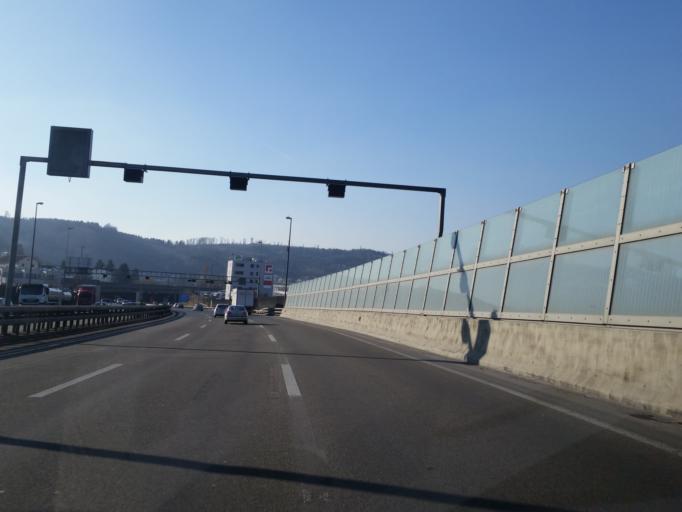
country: CH
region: Aargau
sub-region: Bezirk Baden
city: Neuenhof
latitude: 47.4548
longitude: 8.3301
